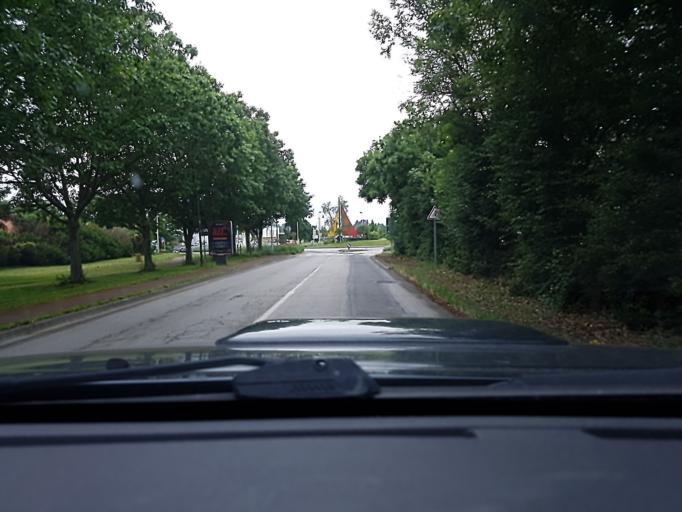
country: FR
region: Pays de la Loire
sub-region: Departement de la Vendee
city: Aizenay
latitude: 46.7368
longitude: -1.6128
